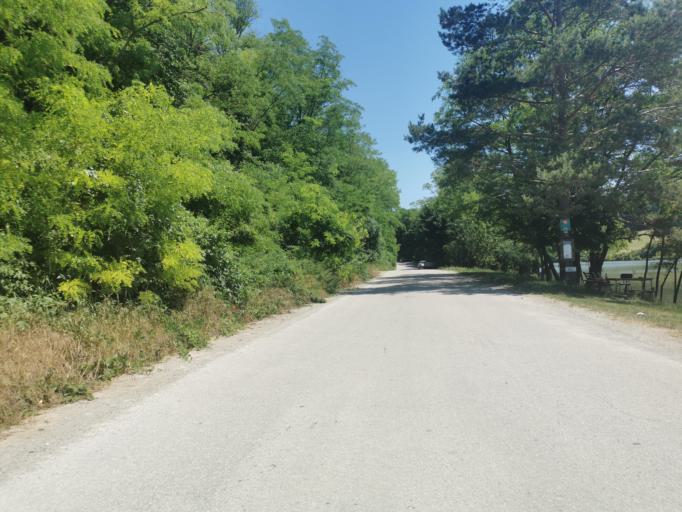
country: SK
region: Trnavsky
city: Smolenice
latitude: 48.5987
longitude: 17.4451
